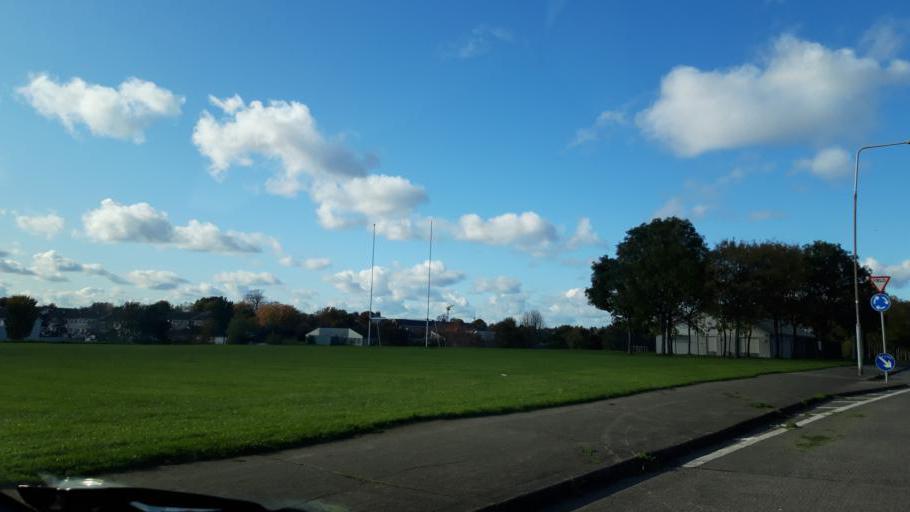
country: IE
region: Leinster
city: Raheny
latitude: 53.3858
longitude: -6.1871
